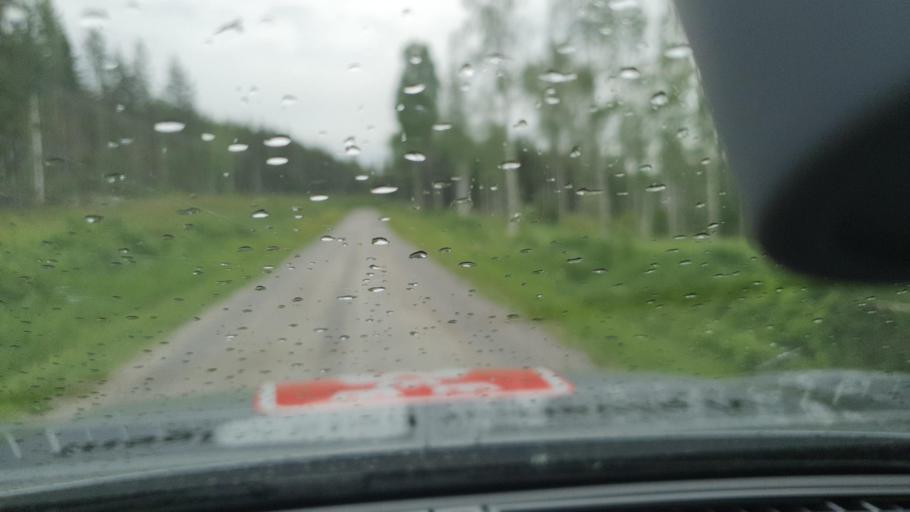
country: SE
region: Norrbotten
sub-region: Kalix Kommun
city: Rolfs
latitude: 66.0176
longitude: 23.1094
